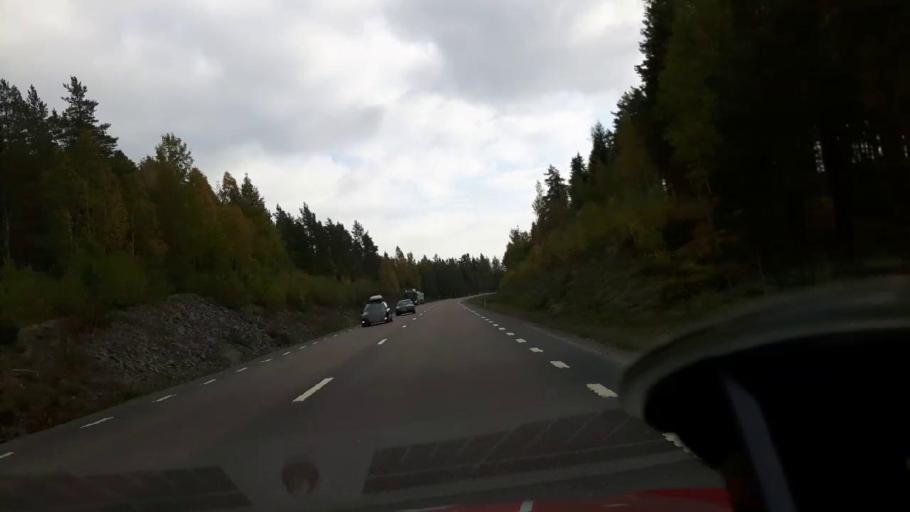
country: SE
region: Gaevleborg
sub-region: Bollnas Kommun
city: Kilafors
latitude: 61.2717
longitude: 16.5349
